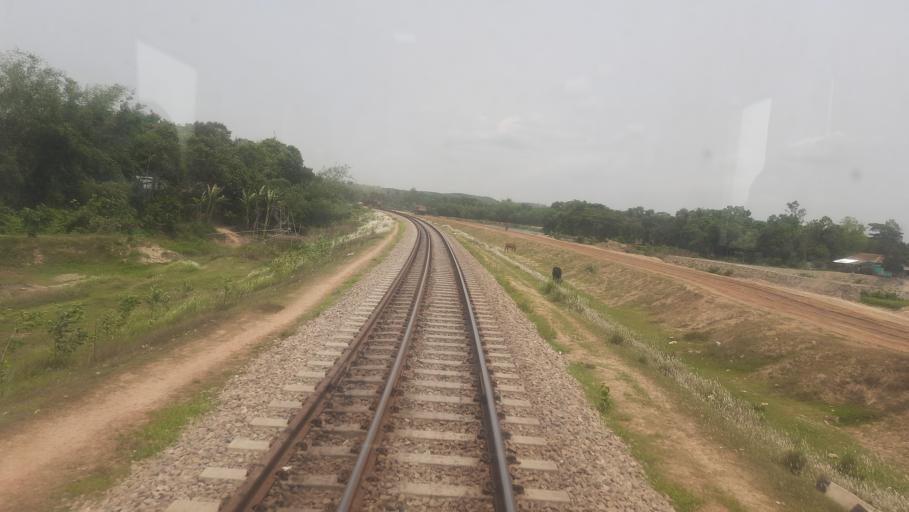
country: IN
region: Tripura
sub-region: West Tripura
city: Agartala
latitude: 23.6777
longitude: 91.1578
